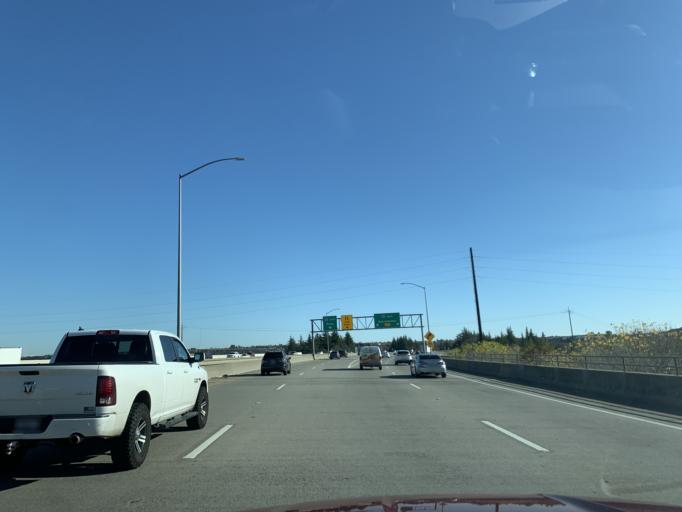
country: US
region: California
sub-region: Placer County
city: Rocklin
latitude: 38.7729
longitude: -121.2544
